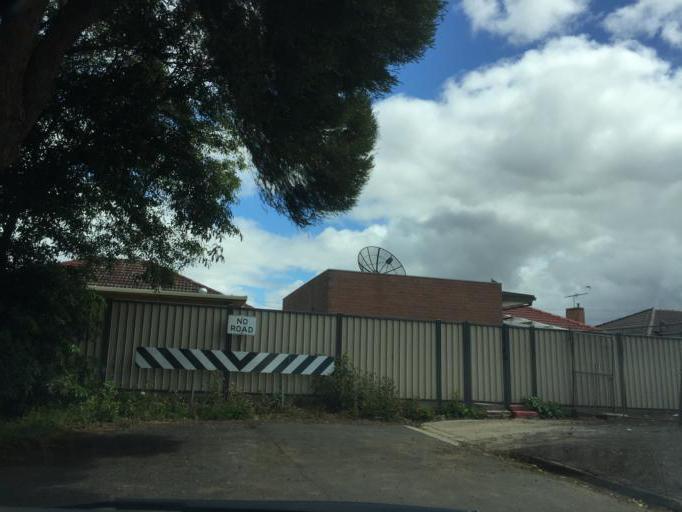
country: AU
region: Victoria
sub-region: Brimbank
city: Albion
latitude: -37.7758
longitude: 144.8424
